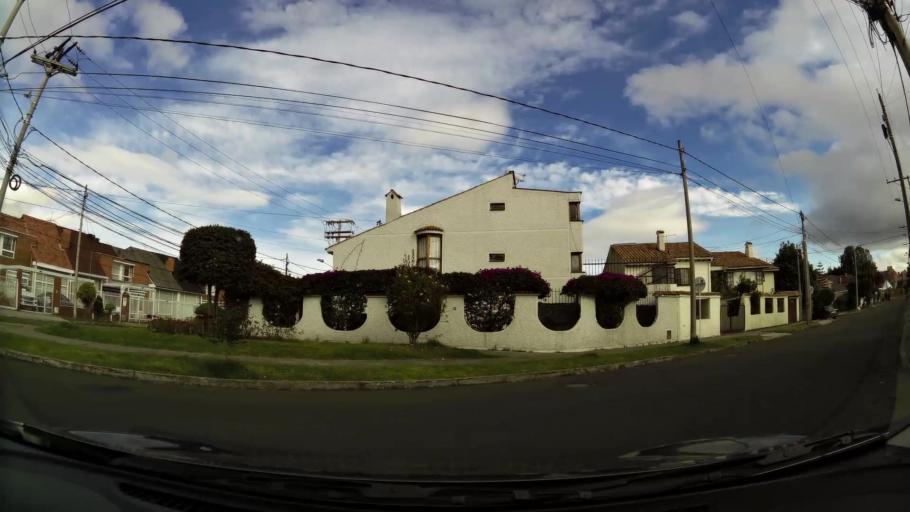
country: CO
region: Bogota D.C.
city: Barrio San Luis
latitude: 4.6926
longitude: -74.0709
